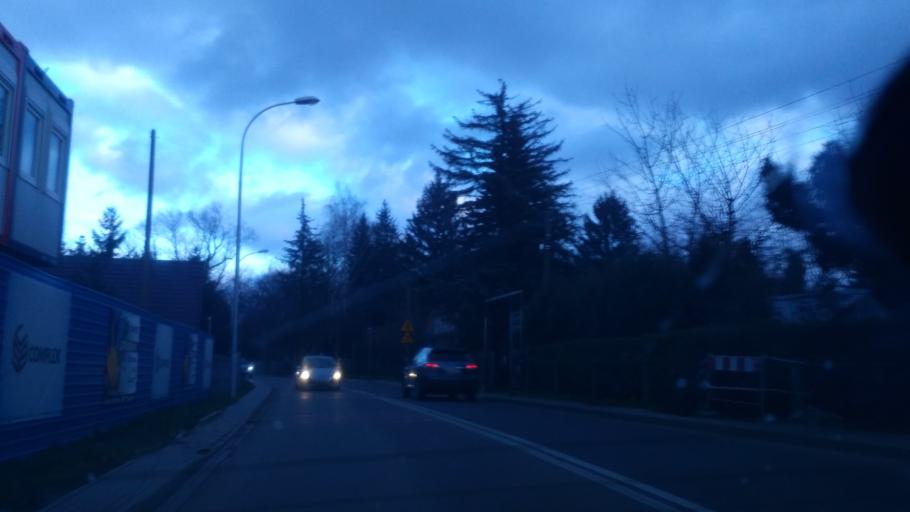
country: PL
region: Subcarpathian Voivodeship
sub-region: Rzeszow
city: Rzeszow
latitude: 50.0265
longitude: 22.0364
